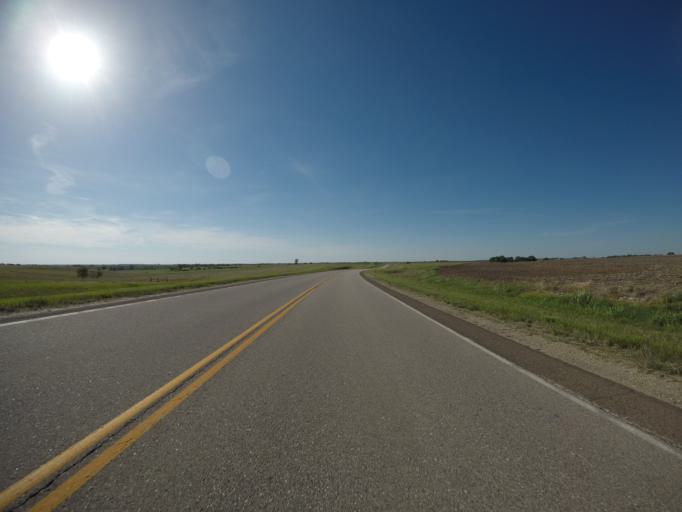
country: US
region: Kansas
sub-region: Clay County
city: Clay Center
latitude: 39.3673
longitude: -96.9483
